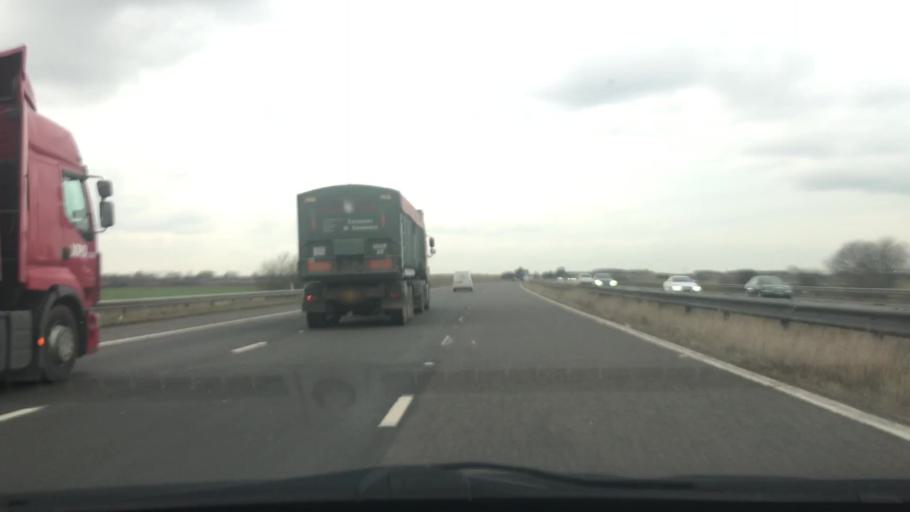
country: GB
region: England
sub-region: Doncaster
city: Hatfield
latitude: 53.5813
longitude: -0.9466
